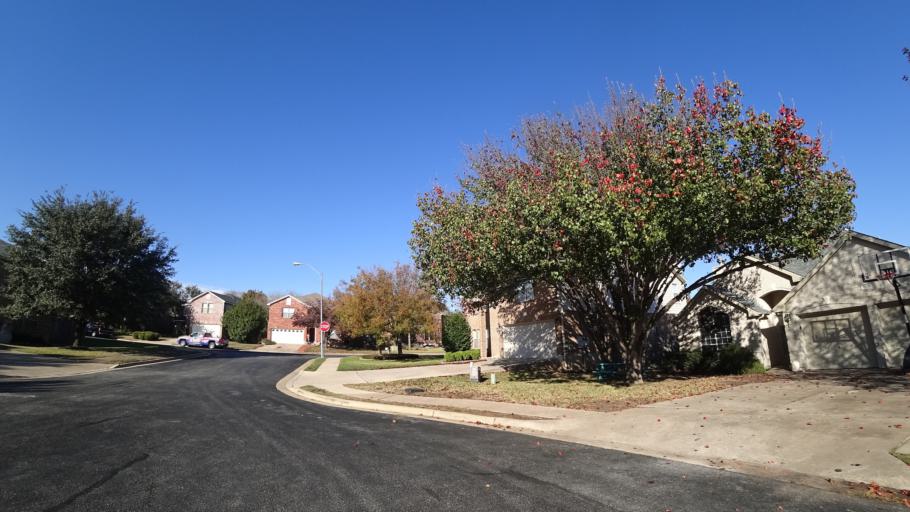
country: US
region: Texas
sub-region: Williamson County
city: Brushy Creek
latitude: 30.4854
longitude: -97.7415
